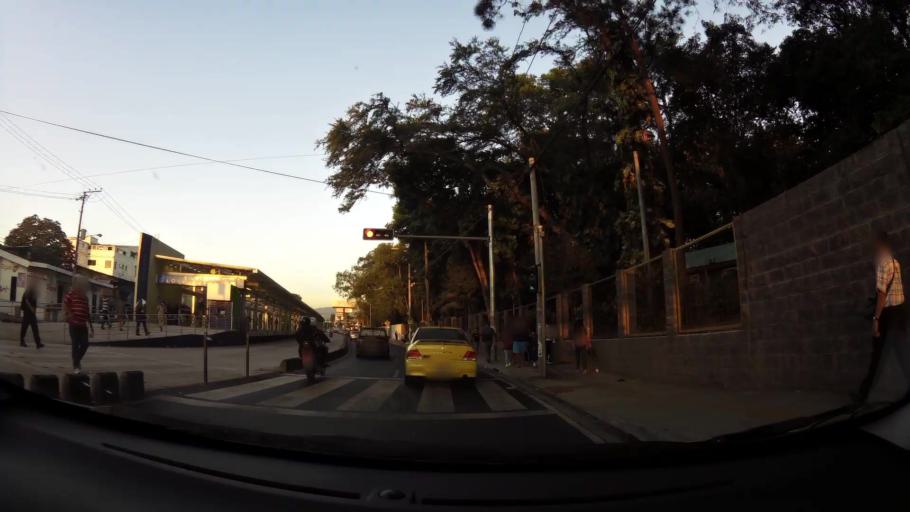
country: SV
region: San Salvador
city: San Salvador
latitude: 13.7031
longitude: -89.1936
